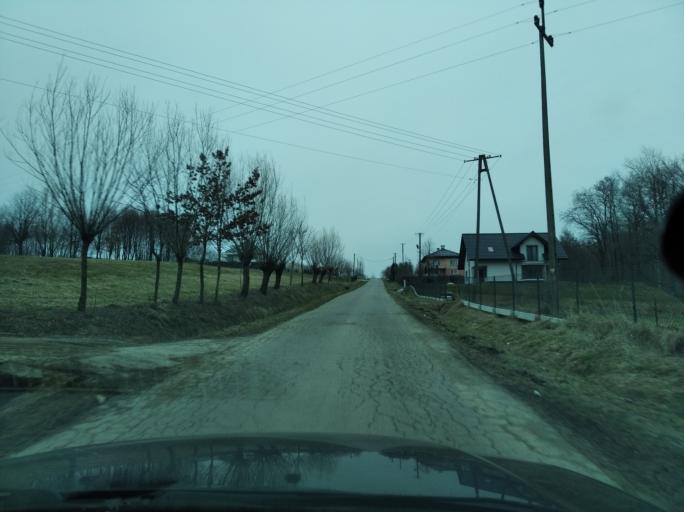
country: PL
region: Subcarpathian Voivodeship
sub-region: Powiat rzeszowski
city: Chmielnik
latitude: 49.9780
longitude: 22.1459
